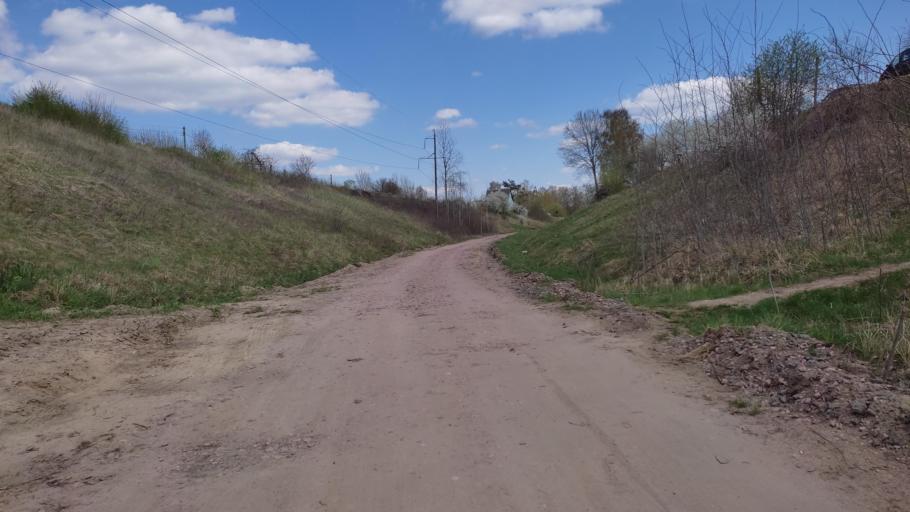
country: BY
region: Grodnenskaya
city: Hrodna
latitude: 53.6583
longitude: 23.8933
